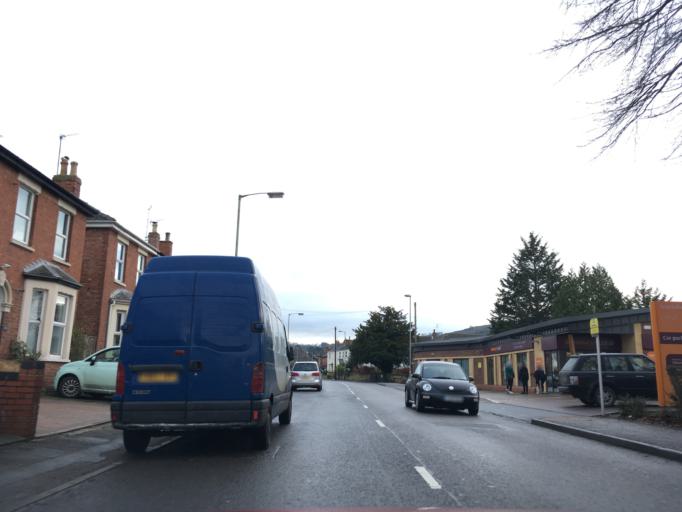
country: GB
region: England
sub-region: Gloucestershire
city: Charlton Kings
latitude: 51.8813
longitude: -2.0553
